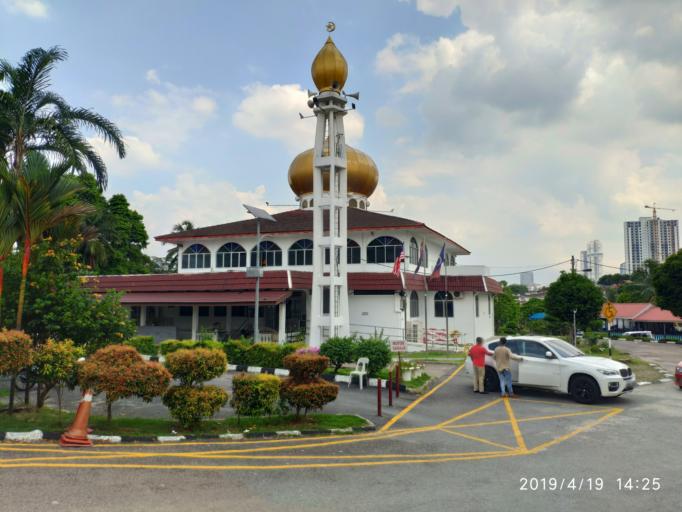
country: MY
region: Johor
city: Johor Bahru
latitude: 1.4818
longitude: 103.7723
